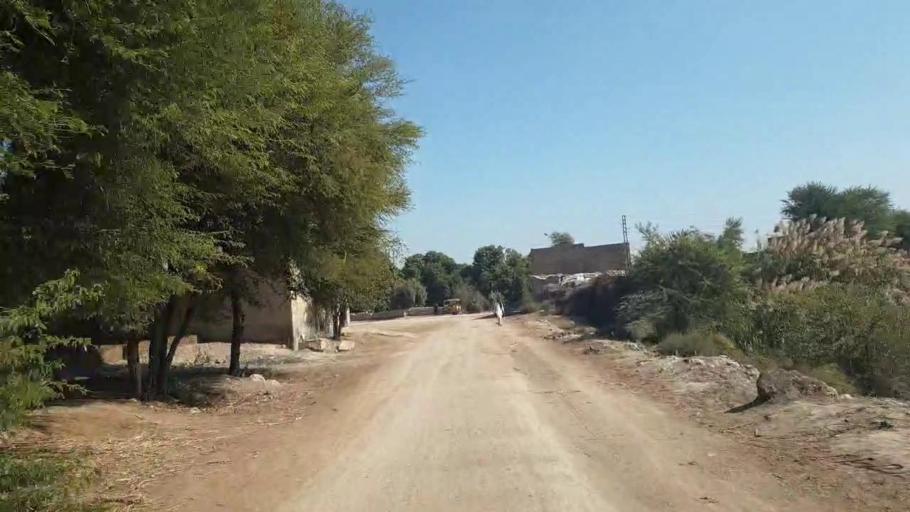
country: PK
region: Sindh
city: Shahpur Chakar
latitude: 26.1057
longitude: 68.6349
